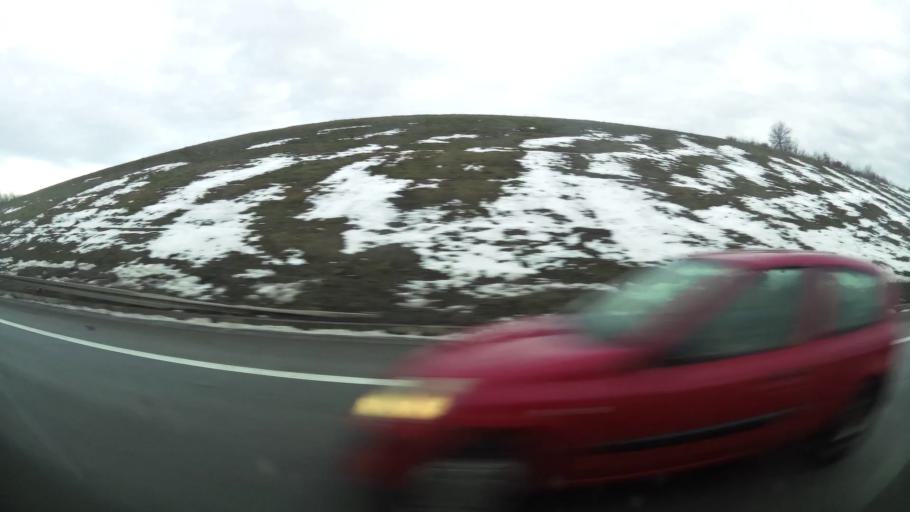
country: RS
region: Central Serbia
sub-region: Belgrade
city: Rakovica
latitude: 44.7152
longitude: 20.4350
